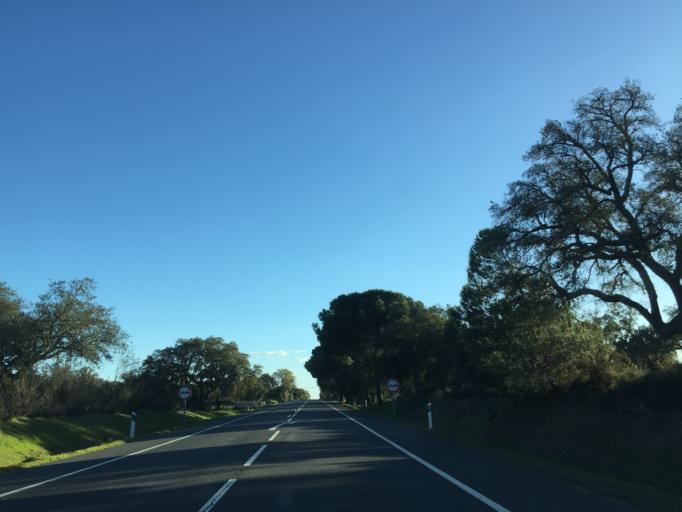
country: PT
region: Setubal
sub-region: Grandola
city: Grandola
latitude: 38.0307
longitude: -8.4001
